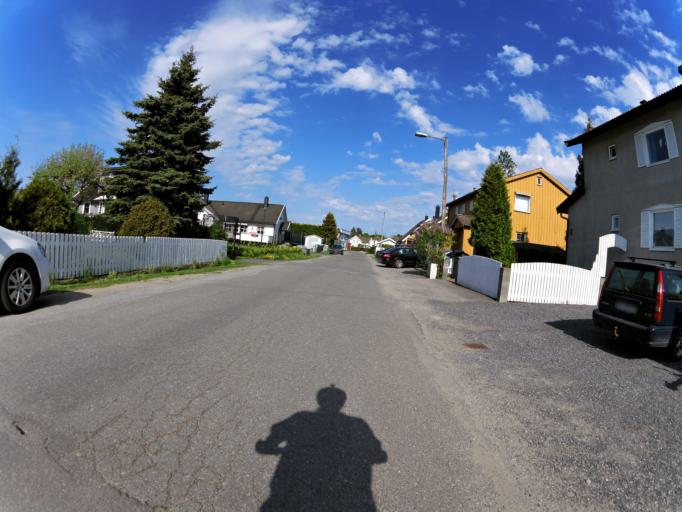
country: NO
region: Ostfold
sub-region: Fredrikstad
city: Fredrikstad
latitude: 59.2329
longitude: 10.9716
